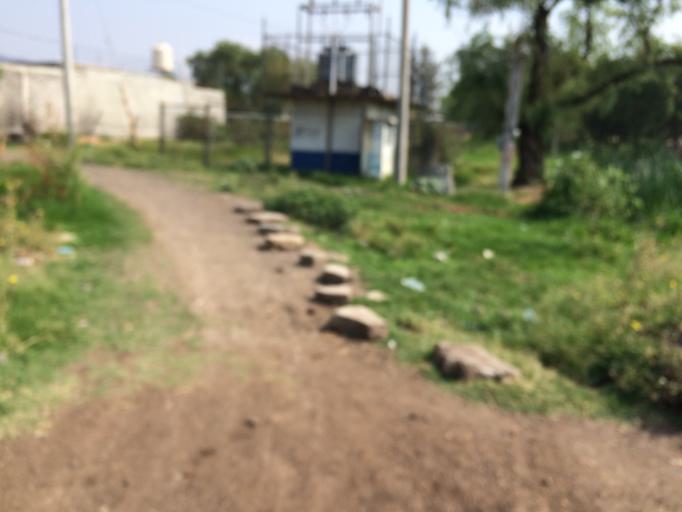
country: MX
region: Michoacan
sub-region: Tarimbaro
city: Real Hacienda (Metropolis)
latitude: 19.7332
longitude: -101.2142
